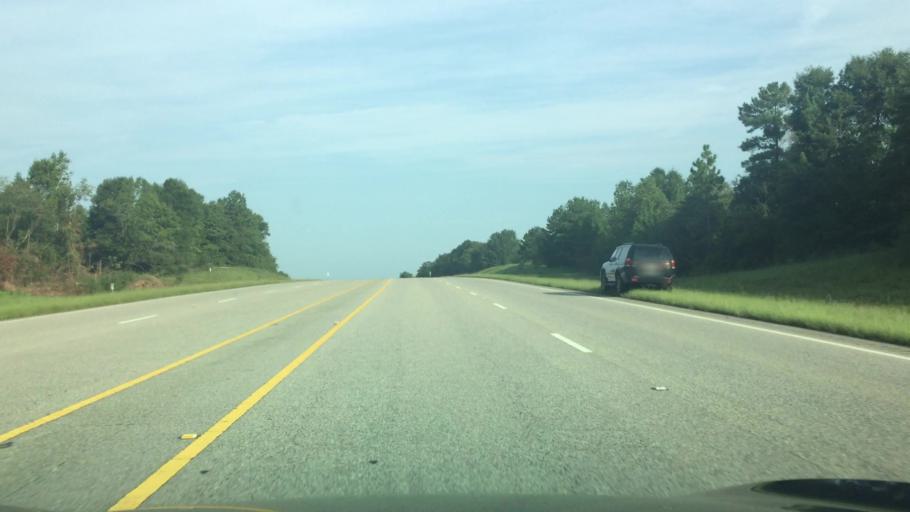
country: US
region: Alabama
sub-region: Butler County
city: Georgiana
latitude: 31.4605
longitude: -86.6426
